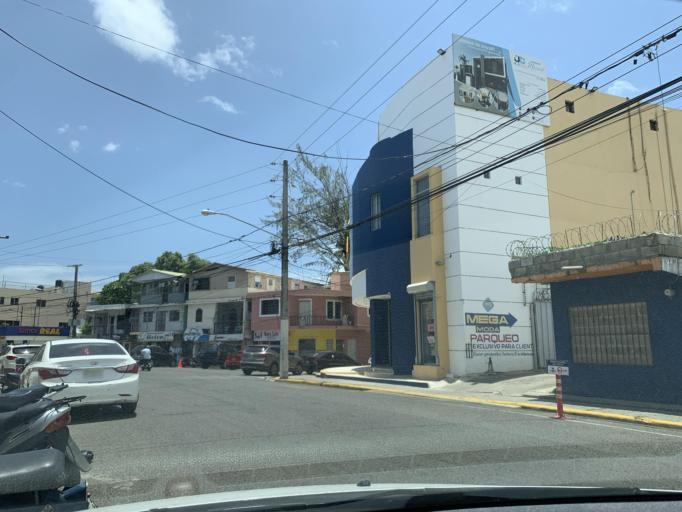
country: DO
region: Puerto Plata
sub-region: Puerto Plata
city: Puerto Plata
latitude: 19.7925
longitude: -70.6969
